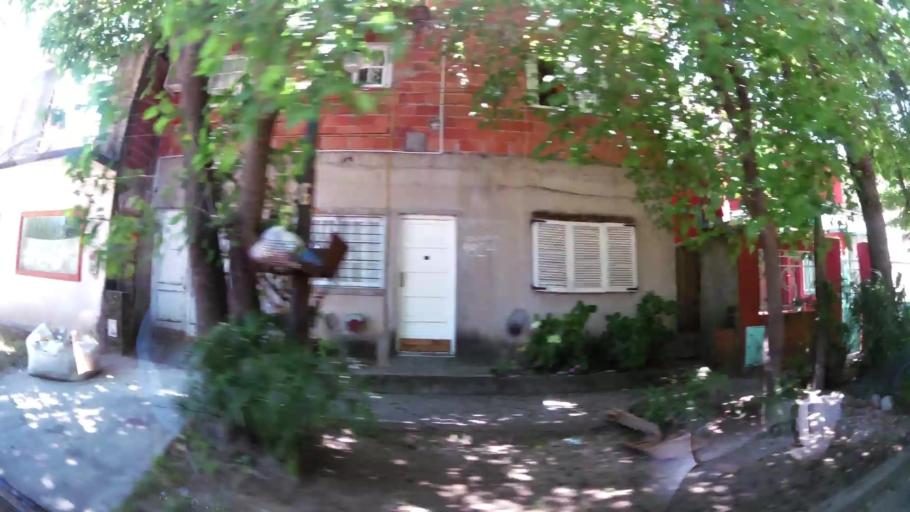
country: AR
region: Buenos Aires
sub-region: Partido de Tigre
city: Tigre
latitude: -34.4424
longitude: -58.5453
